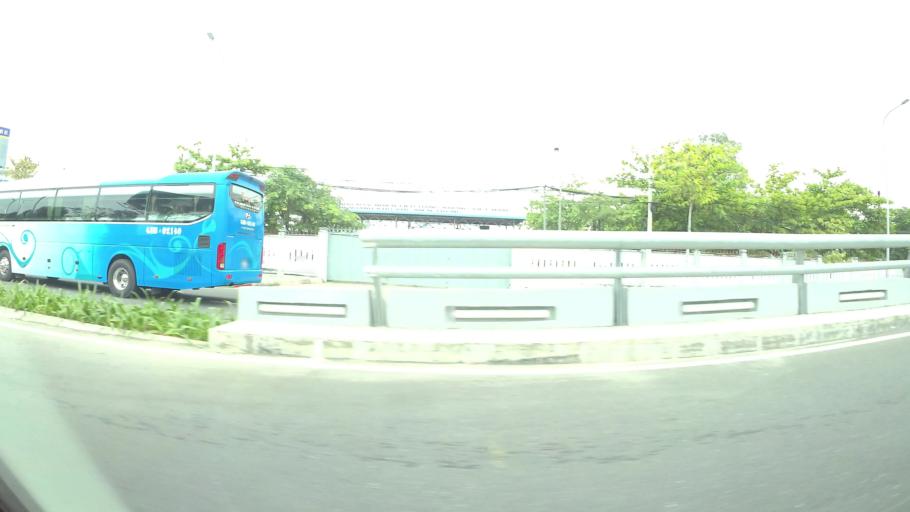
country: VN
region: Da Nang
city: Thanh Khe
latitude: 16.0570
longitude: 108.2038
